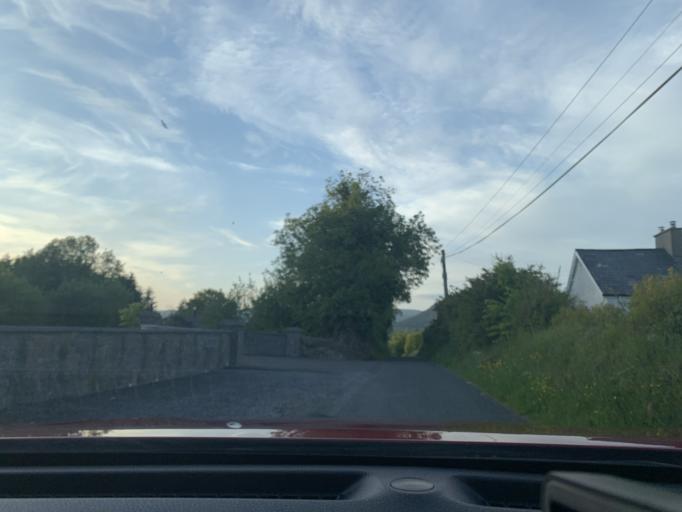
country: IE
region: Connaught
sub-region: Sligo
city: Sligo
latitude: 54.2874
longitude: -8.4310
